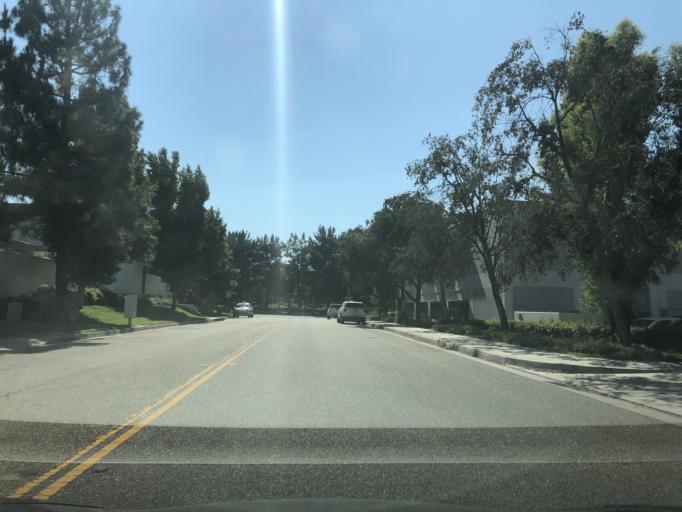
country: US
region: California
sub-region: Riverside County
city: El Cerrito
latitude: 33.8578
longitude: -117.5381
